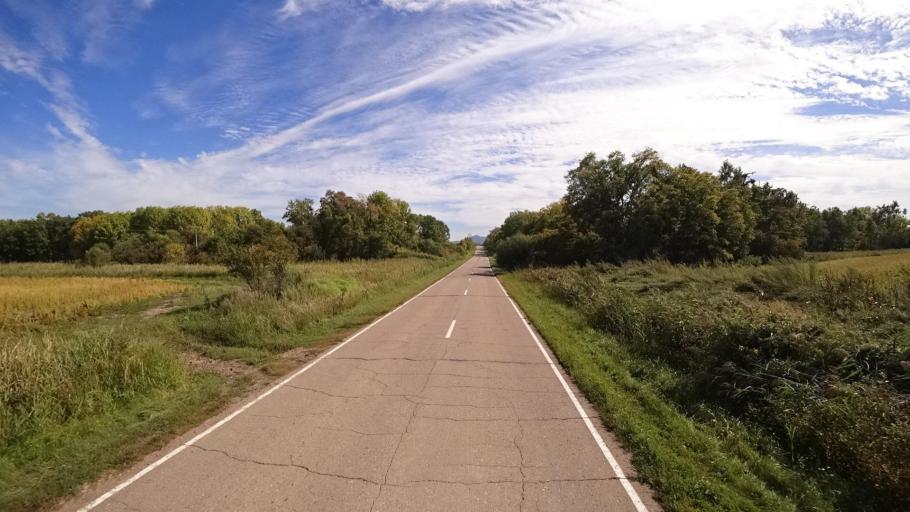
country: RU
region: Primorskiy
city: Yakovlevka
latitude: 44.4206
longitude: 133.5792
